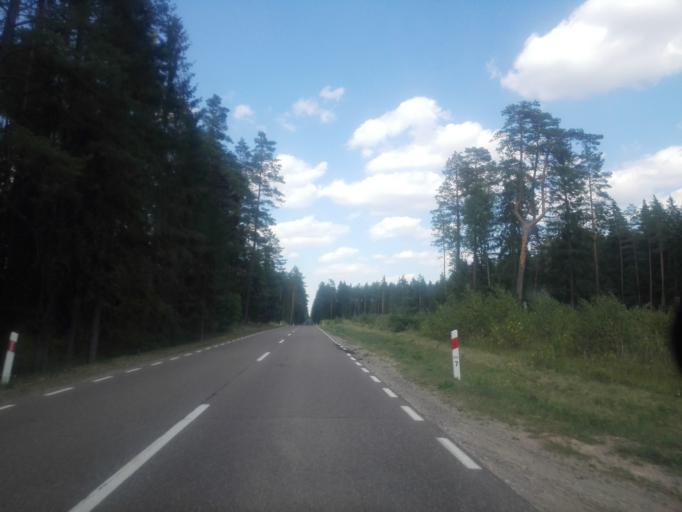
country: PL
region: Podlasie
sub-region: Powiat augustowski
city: Augustow
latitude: 53.9207
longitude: 23.1519
